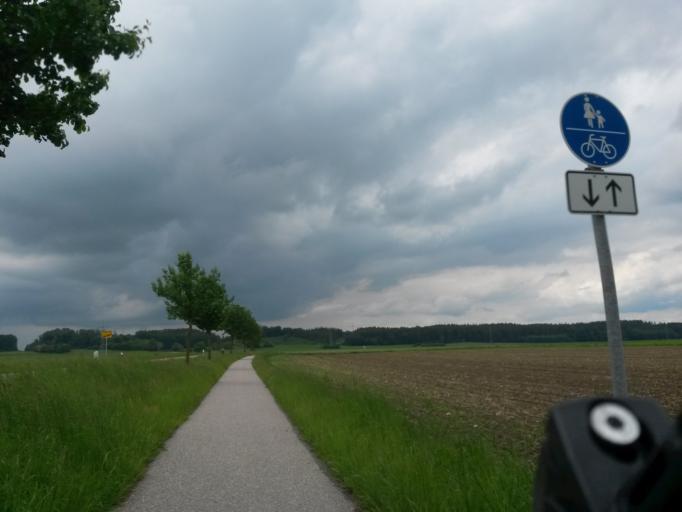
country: DE
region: Baden-Wuerttemberg
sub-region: Tuebingen Region
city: Bad Waldsee
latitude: 47.9212
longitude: 9.7975
